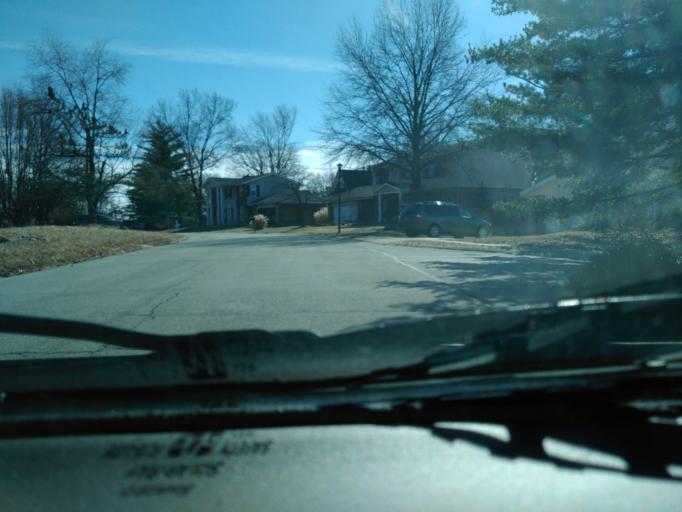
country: US
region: Missouri
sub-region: Saint Louis County
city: Ballwin
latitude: 38.5986
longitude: -90.5441
